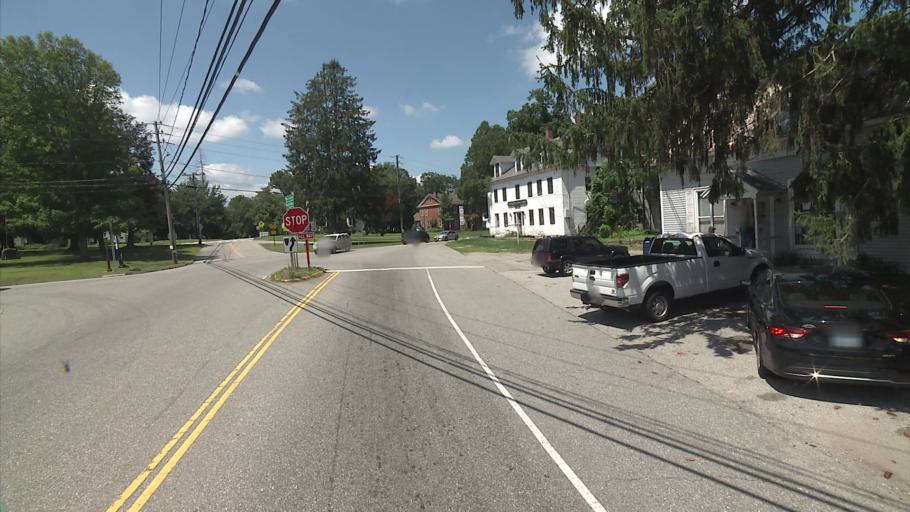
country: US
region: Connecticut
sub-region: Windham County
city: Windham
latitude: 41.6998
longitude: -72.1573
